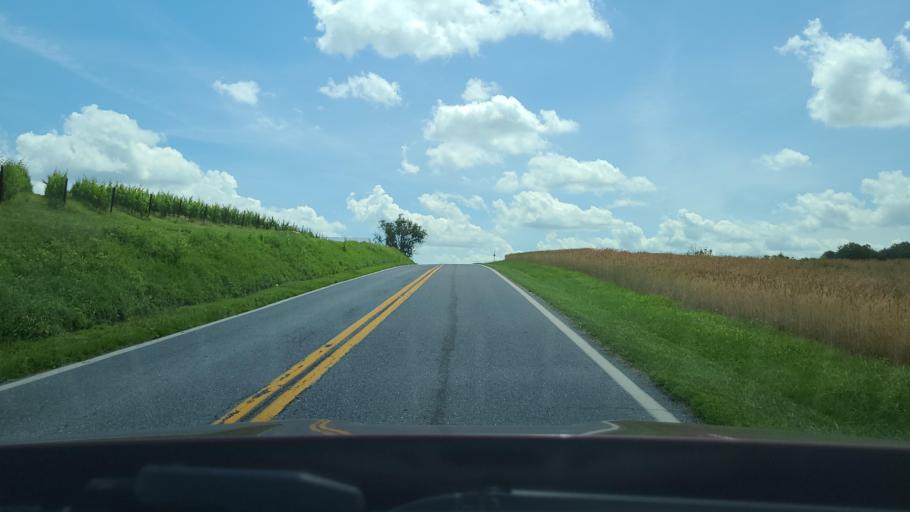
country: US
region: Maryland
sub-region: Montgomery County
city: Clarksburg
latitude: 39.2690
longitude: -77.2526
